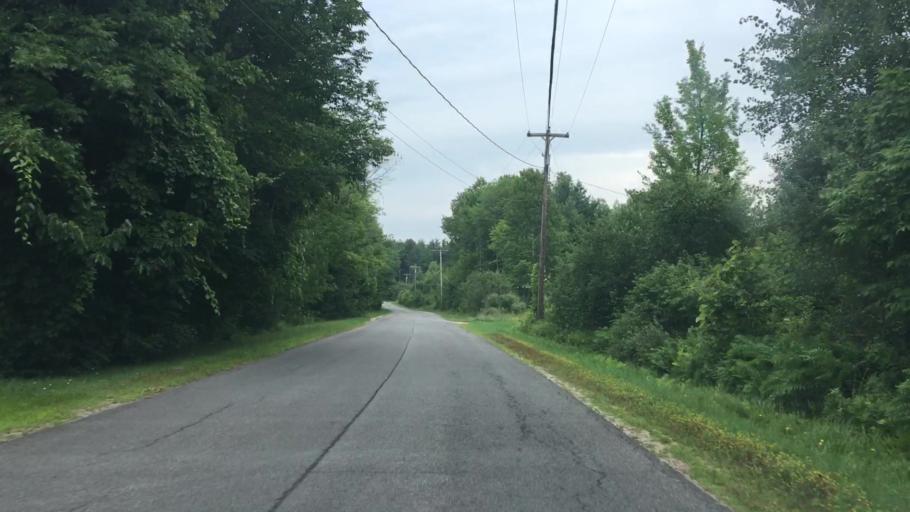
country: US
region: New York
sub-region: Clinton County
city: Peru
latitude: 44.6022
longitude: -73.6035
